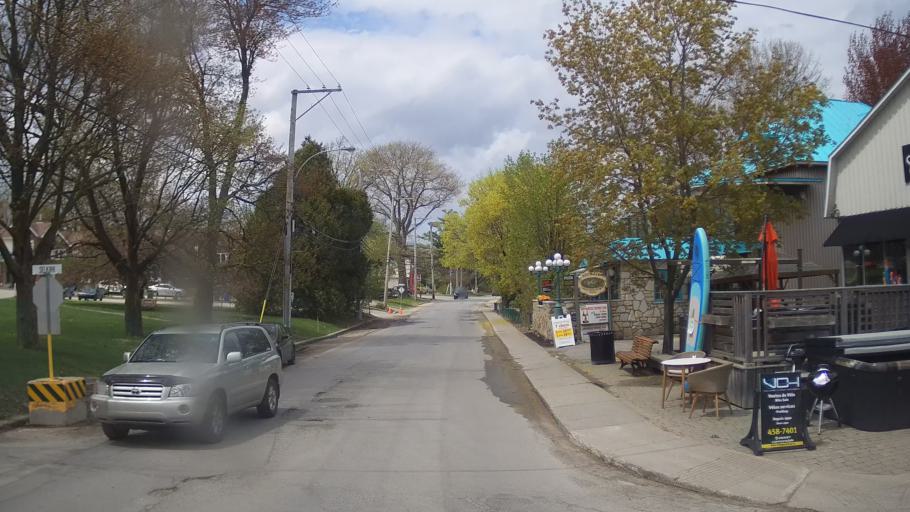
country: CA
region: Quebec
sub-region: Monteregie
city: Hudson
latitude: 45.4597
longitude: -74.1441
